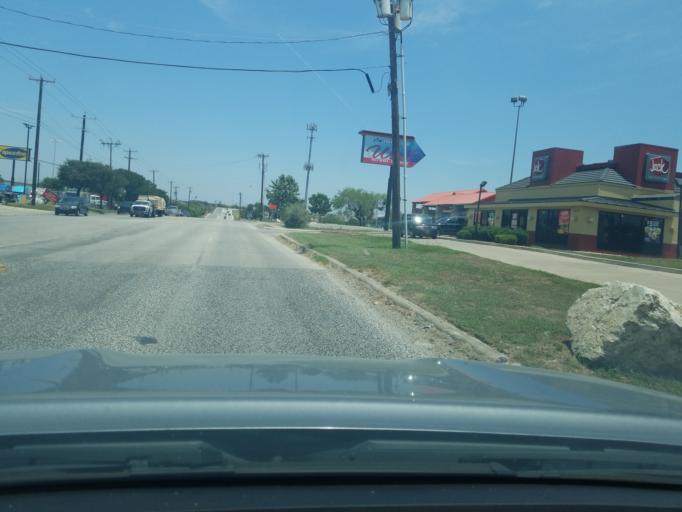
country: US
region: Texas
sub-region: Bexar County
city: Kirby
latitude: 29.4465
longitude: -98.3608
